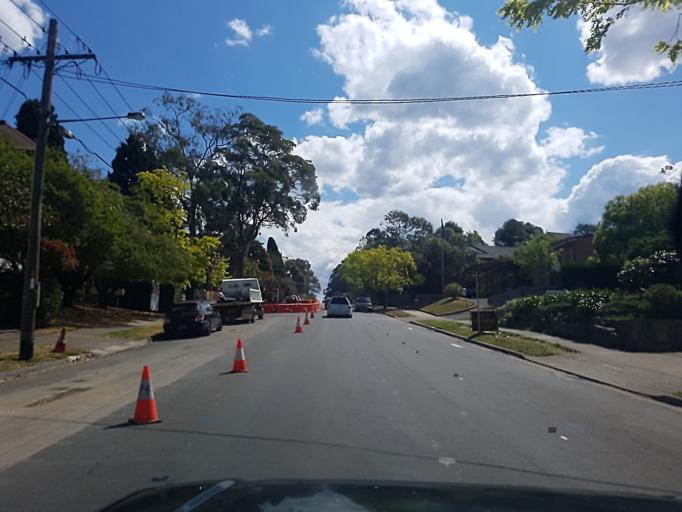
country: AU
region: New South Wales
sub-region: Hornsby Shire
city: Hornsby
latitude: -33.7032
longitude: 151.1057
